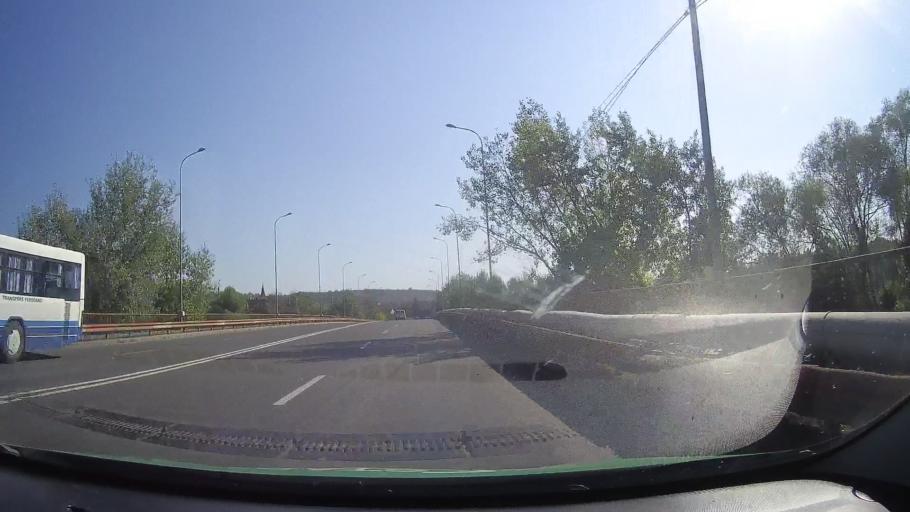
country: RO
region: Arad
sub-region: Oras Lipova
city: Radna
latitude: 46.0916
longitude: 21.6878
